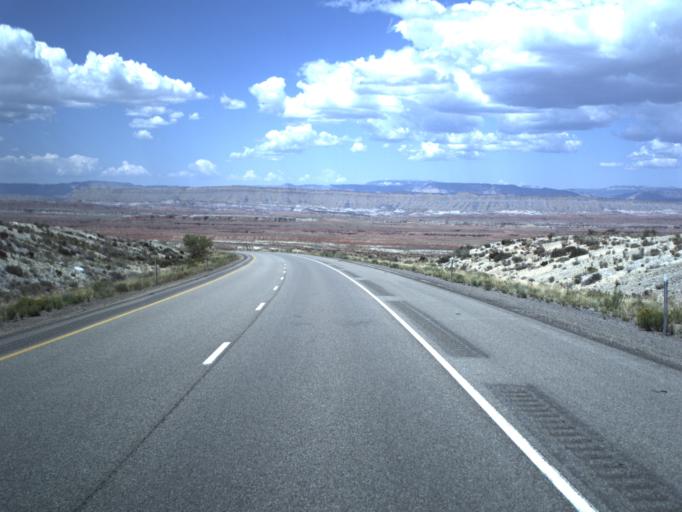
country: US
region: Utah
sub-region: Emery County
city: Ferron
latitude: 38.8458
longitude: -110.9892
